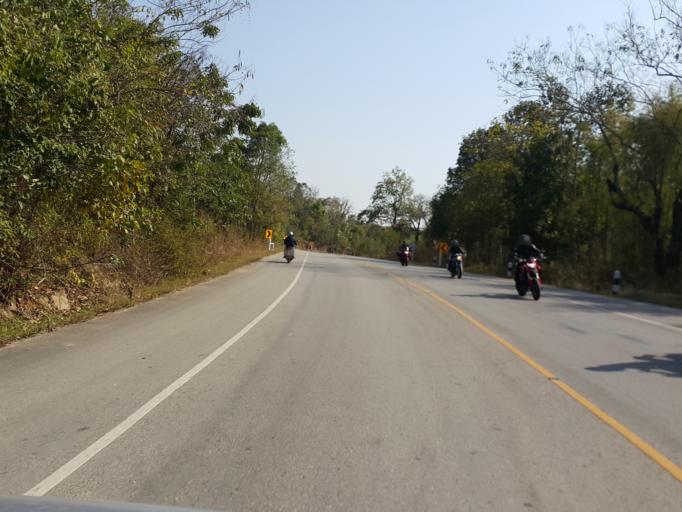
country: TH
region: Lampang
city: Chae Hom
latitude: 18.7680
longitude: 99.5729
